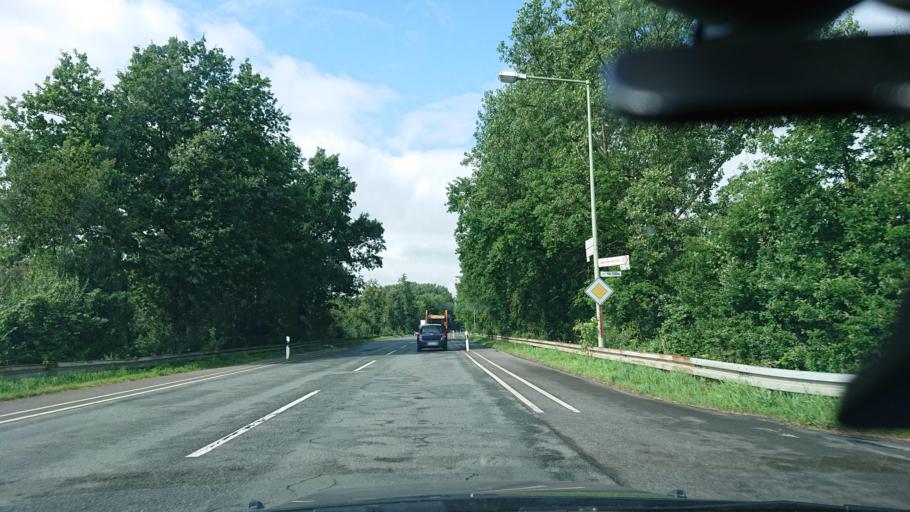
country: DE
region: North Rhine-Westphalia
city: Lunen
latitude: 51.6163
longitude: 7.5612
